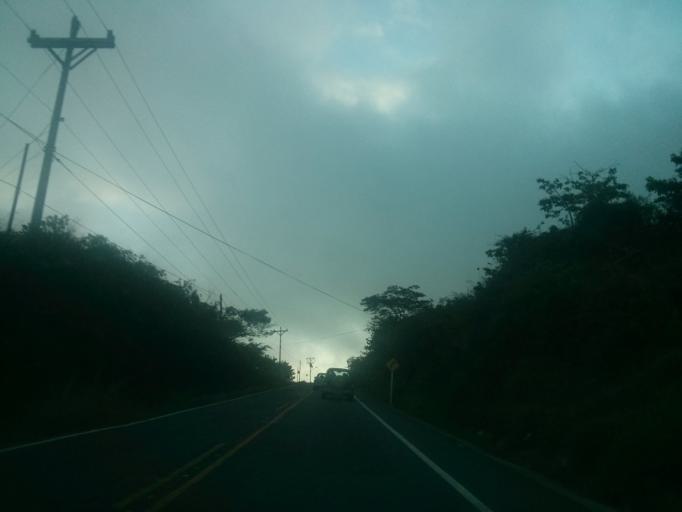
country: CR
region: Cartago
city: Cot
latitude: 9.8867
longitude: -83.8750
